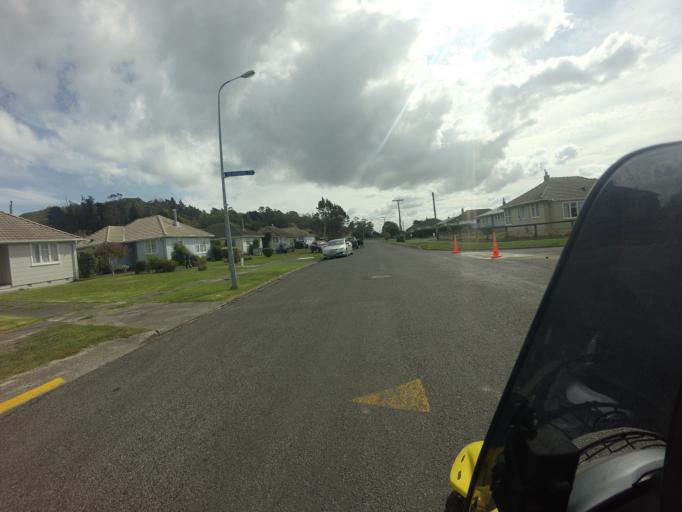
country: NZ
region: Gisborne
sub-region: Gisborne District
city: Gisborne
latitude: -38.6752
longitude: 178.0380
